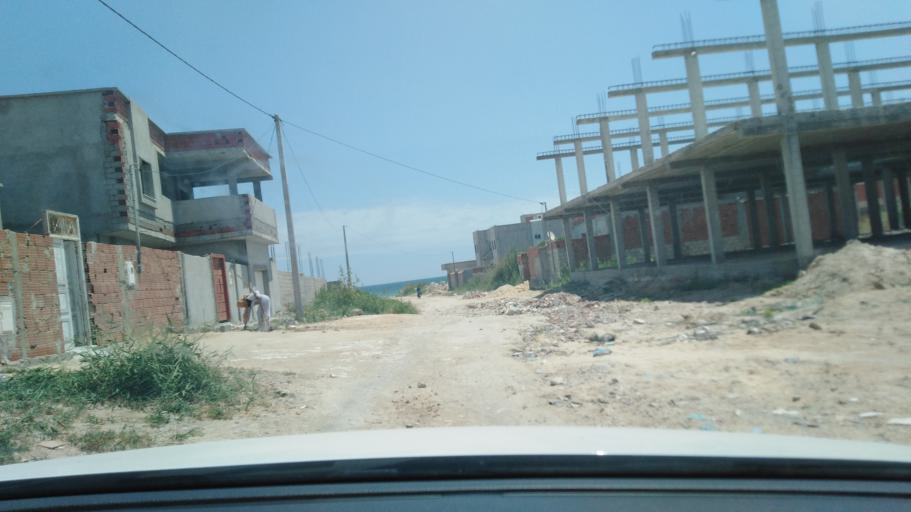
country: TN
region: Qabis
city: Gabes
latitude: 33.9463
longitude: 10.0730
